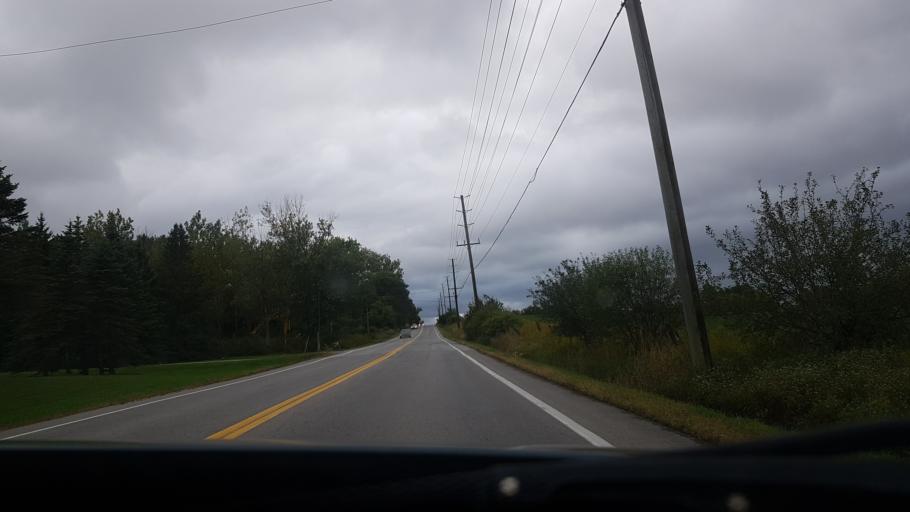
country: CA
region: Ontario
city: Newmarket
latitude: 44.0541
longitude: -79.3967
